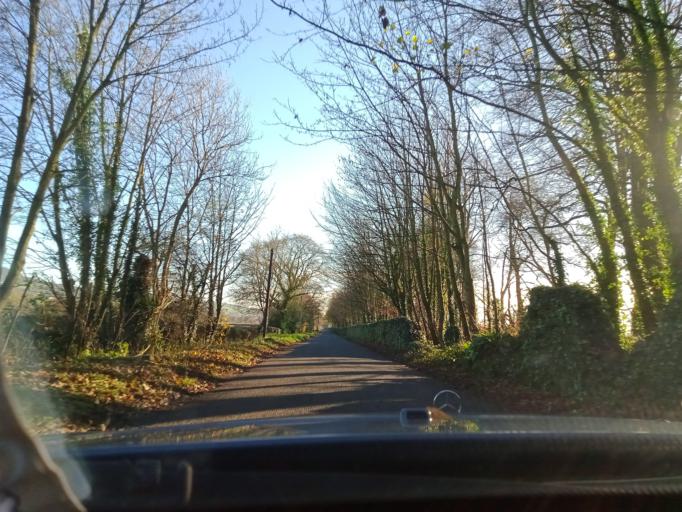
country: IE
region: Leinster
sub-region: Kilkenny
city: Piltown
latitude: 52.3624
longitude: -7.3148
